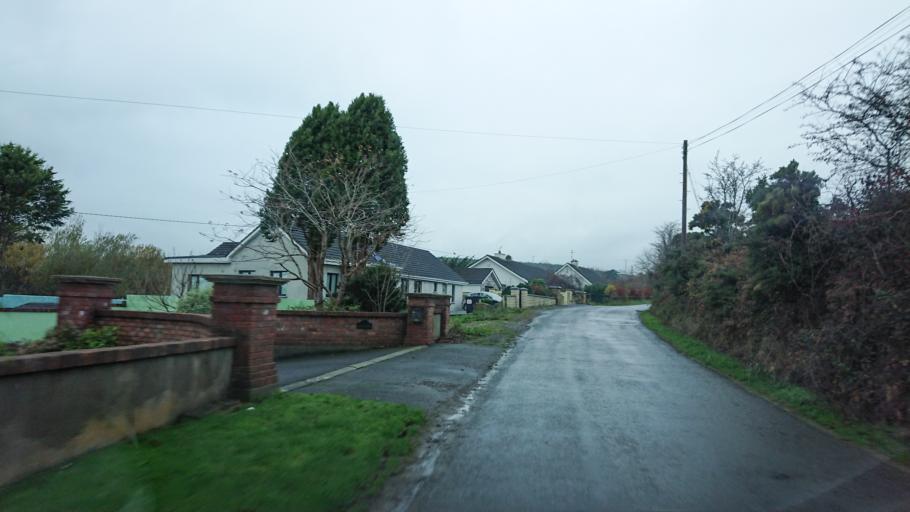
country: IE
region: Munster
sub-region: Waterford
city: Tra Mhor
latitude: 52.1956
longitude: -7.1266
